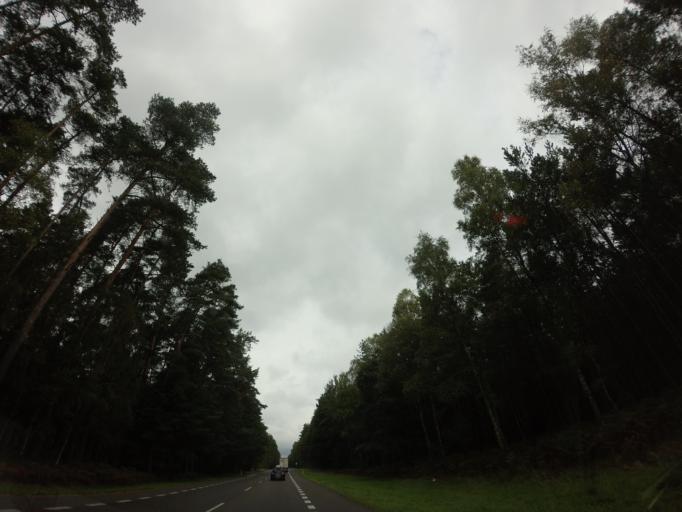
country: PL
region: West Pomeranian Voivodeship
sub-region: Powiat goleniowski
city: Przybiernow
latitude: 53.6979
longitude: 14.7885
